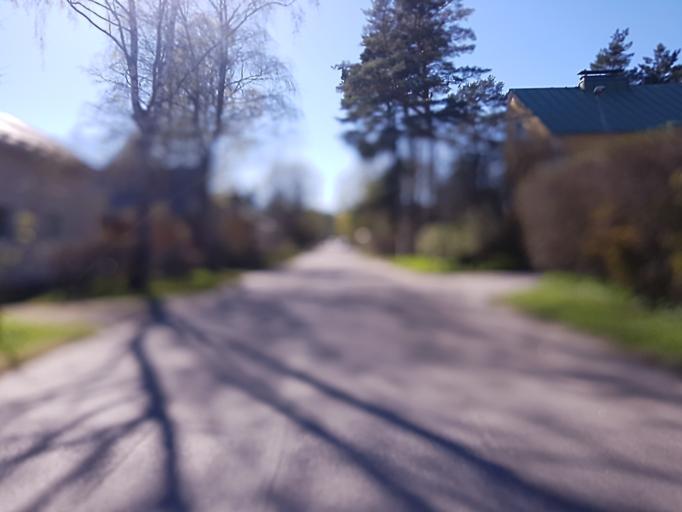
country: FI
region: Uusimaa
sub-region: Helsinki
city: Helsinki
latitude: 60.2446
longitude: 24.9162
